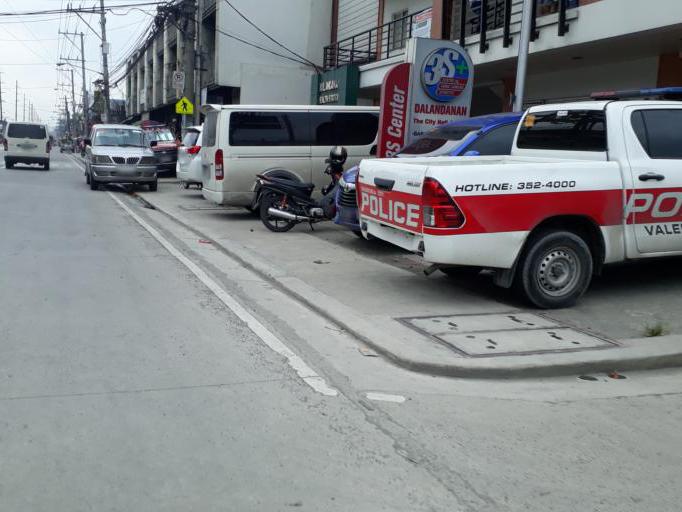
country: PH
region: Calabarzon
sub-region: Province of Rizal
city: Valenzuela
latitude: 14.7044
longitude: 120.9613
